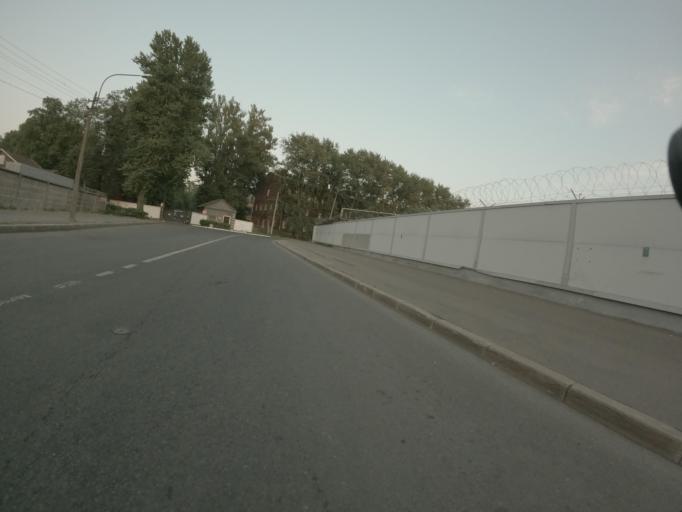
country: RU
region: St.-Petersburg
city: Kupchino
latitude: 59.8930
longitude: 30.3376
